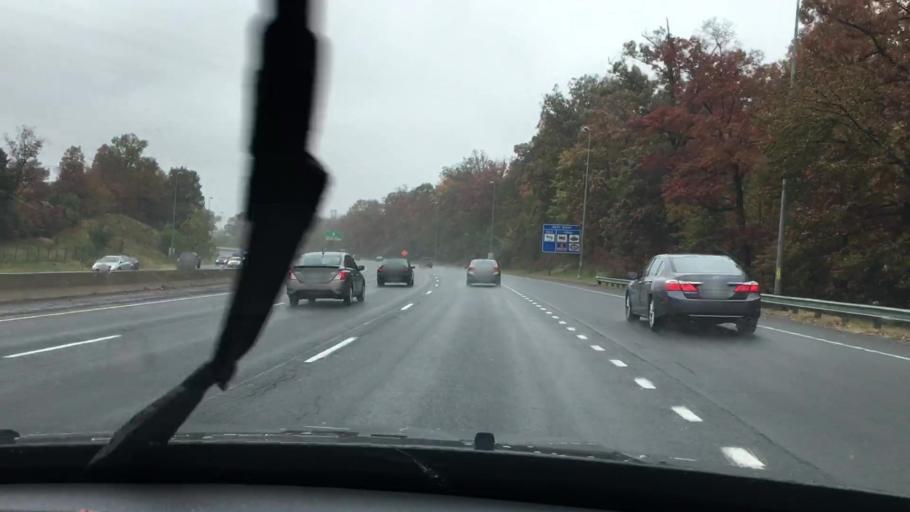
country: US
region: Virginia
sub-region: Fairfax County
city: Chantilly
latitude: 38.8820
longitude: -77.4494
